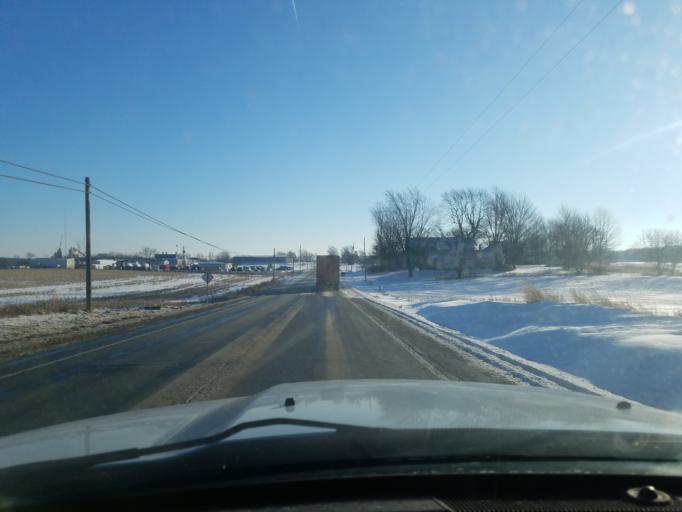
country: US
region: Indiana
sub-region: Noble County
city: Kendallville
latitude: 41.4524
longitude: -85.3157
